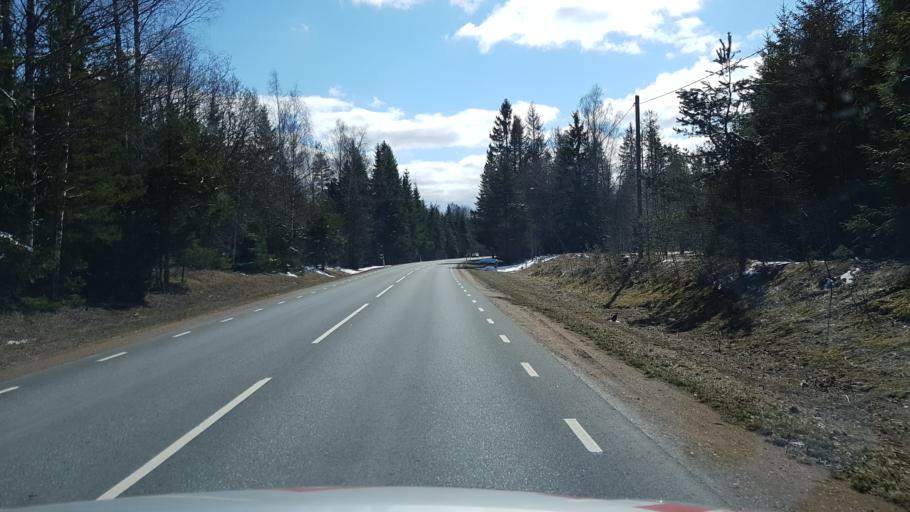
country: EE
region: Laeaene-Virumaa
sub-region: Kadrina vald
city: Kadrina
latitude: 59.3909
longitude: 26.0154
